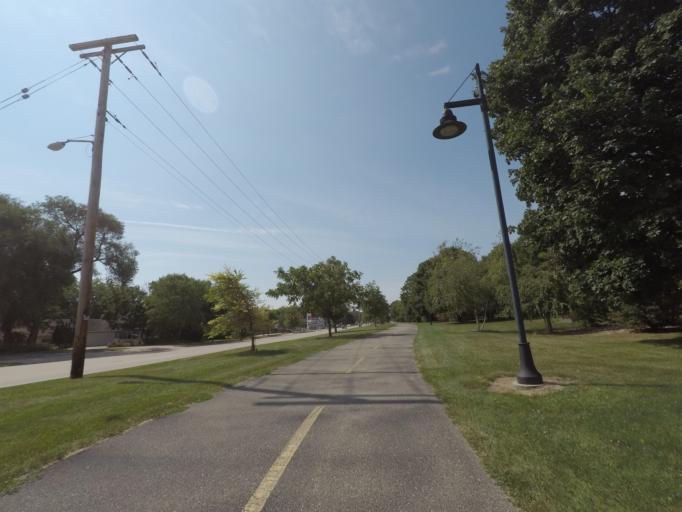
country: US
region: Wisconsin
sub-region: Jefferson County
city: Fort Atkinson
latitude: 42.9248
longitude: -88.8423
